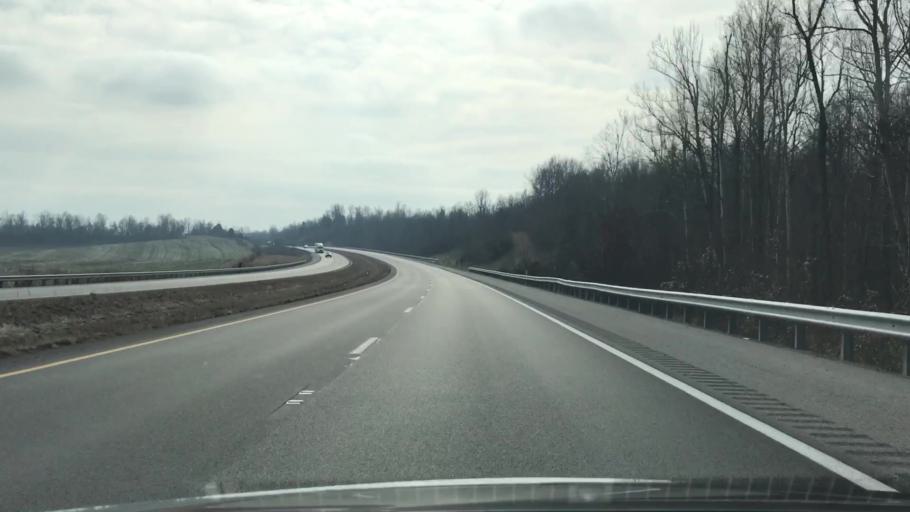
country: US
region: Kentucky
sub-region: Hopkins County
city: Madisonville
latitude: 37.4668
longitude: -87.4800
